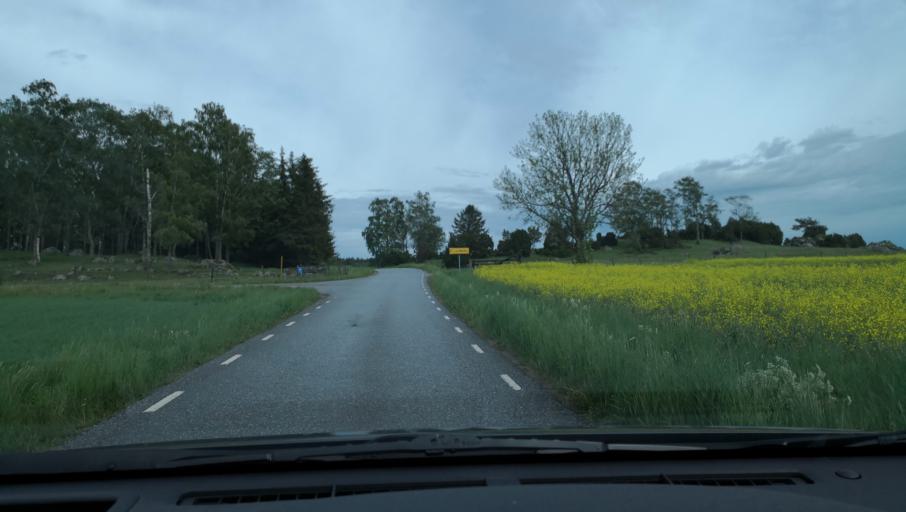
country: SE
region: Uppsala
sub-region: Enkopings Kommun
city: Orsundsbro
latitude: 59.7058
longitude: 17.3695
